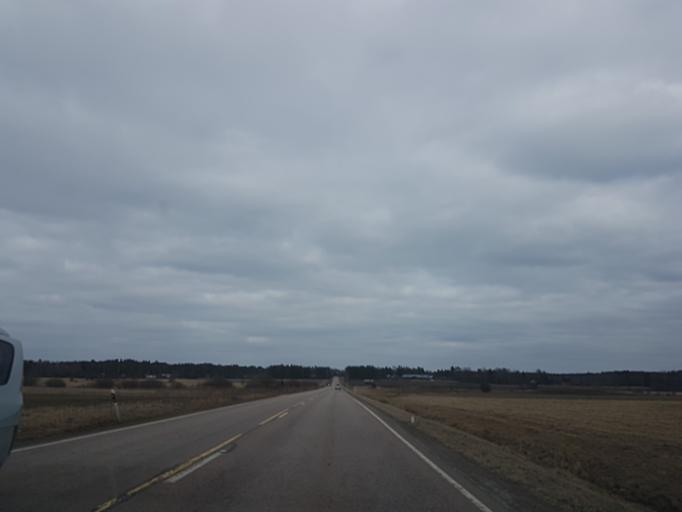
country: FI
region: Kymenlaakso
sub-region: Kotka-Hamina
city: Hamina
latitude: 60.6195
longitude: 27.1983
